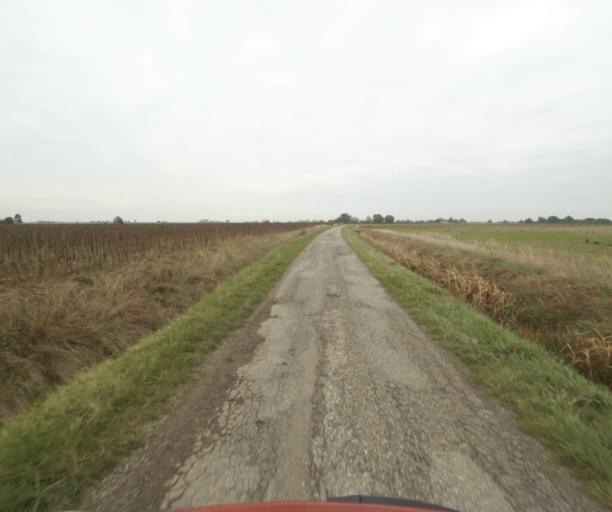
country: FR
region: Midi-Pyrenees
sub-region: Departement de la Haute-Garonne
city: Launac
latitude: 43.8053
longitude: 1.1839
